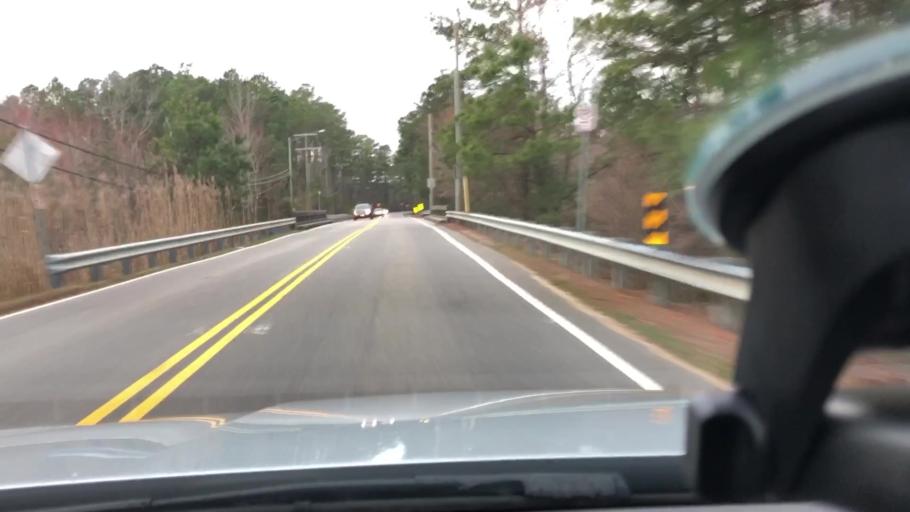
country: US
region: Virginia
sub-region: City of Virginia Beach
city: Virginia Beach
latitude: 36.7332
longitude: -75.9707
